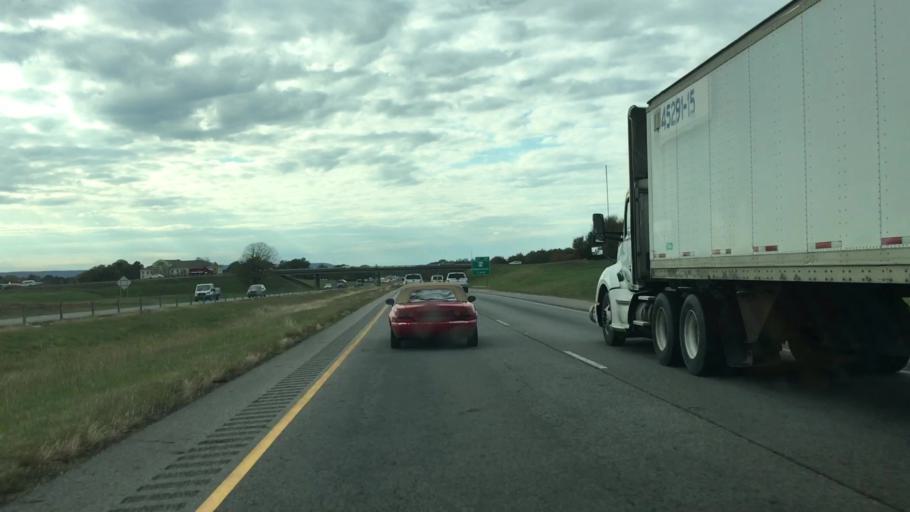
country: US
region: Arkansas
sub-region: Conway County
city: Morrilton
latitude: 35.1742
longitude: -92.7145
